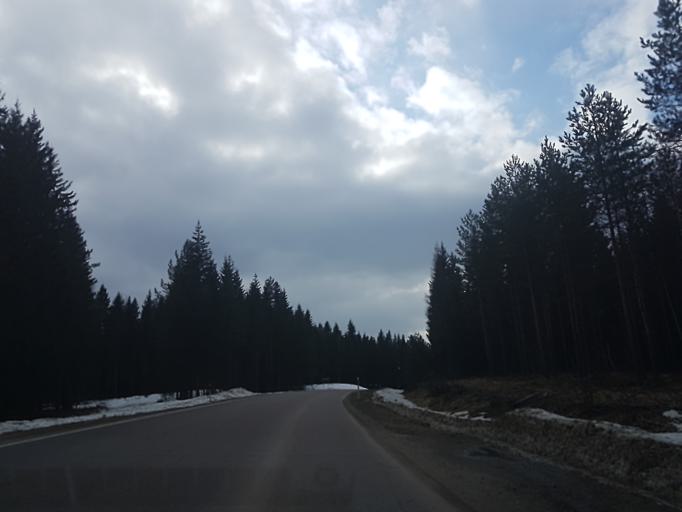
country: FI
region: South Karelia
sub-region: Imatra
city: Parikkala
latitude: 61.5092
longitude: 29.5999
